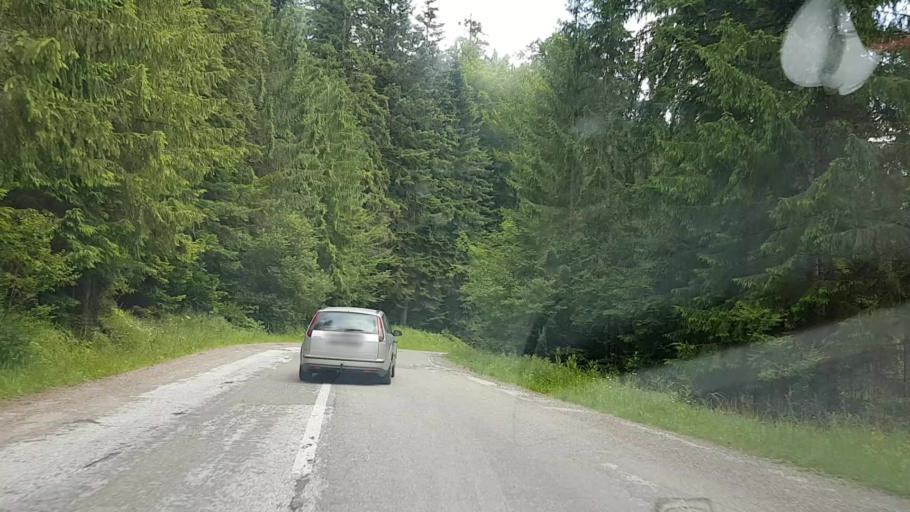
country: RO
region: Neamt
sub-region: Comuna Pangarati
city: Pangarati
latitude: 46.9710
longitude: 26.1173
